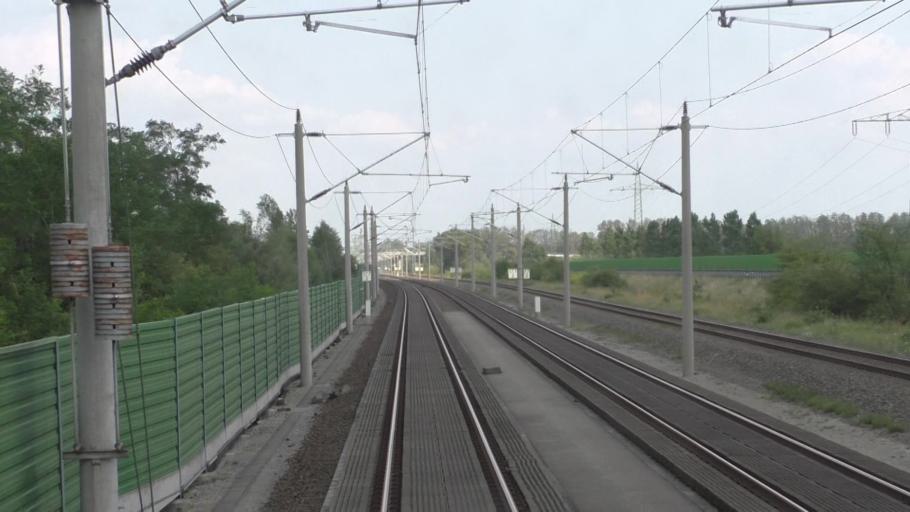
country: DE
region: Brandenburg
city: Rathenow
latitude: 52.5906
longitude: 12.2605
